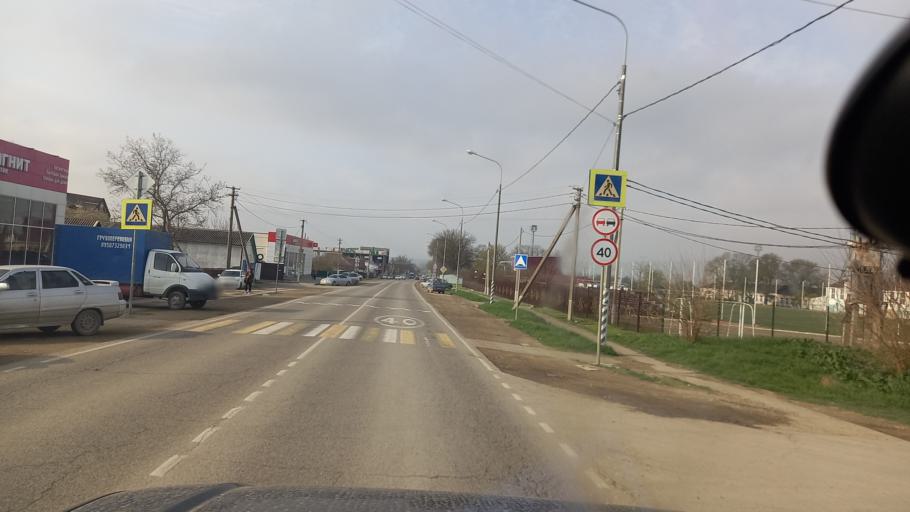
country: RU
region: Krasnodarskiy
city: Varenikovskaya
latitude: 45.1194
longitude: 37.6190
